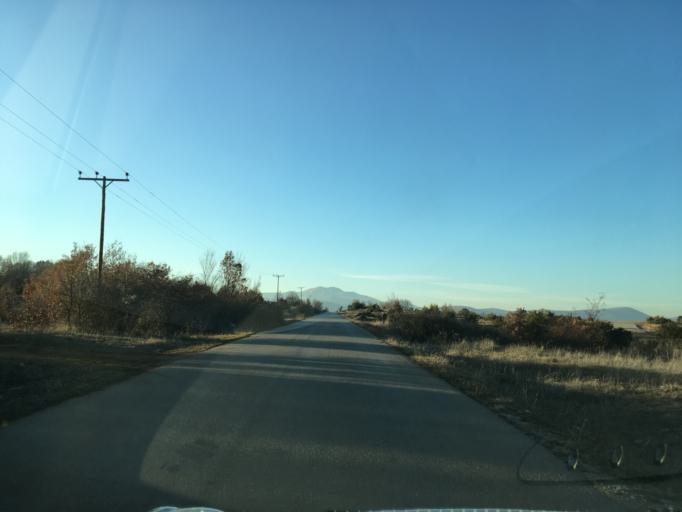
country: GR
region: West Macedonia
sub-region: Nomos Kozanis
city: Kozani
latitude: 40.2693
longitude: 21.7418
